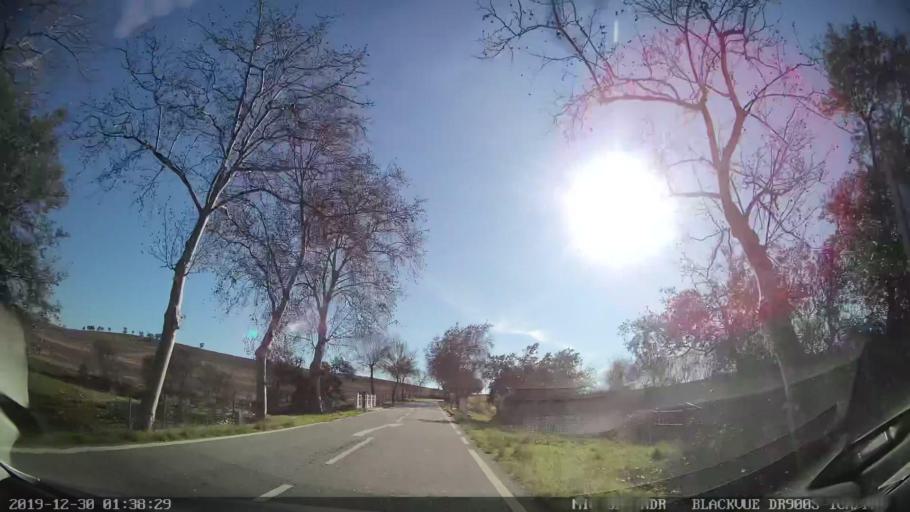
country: PT
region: Castelo Branco
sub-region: Idanha-A-Nova
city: Idanha-a-Nova
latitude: 39.8924
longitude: -7.2070
